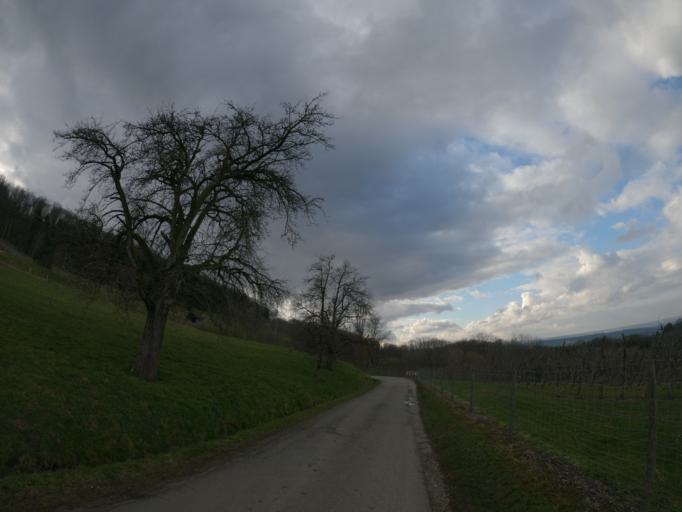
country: DE
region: Baden-Wuerttemberg
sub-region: Regierungsbezirk Stuttgart
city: Schlat
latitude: 48.6538
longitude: 9.6906
